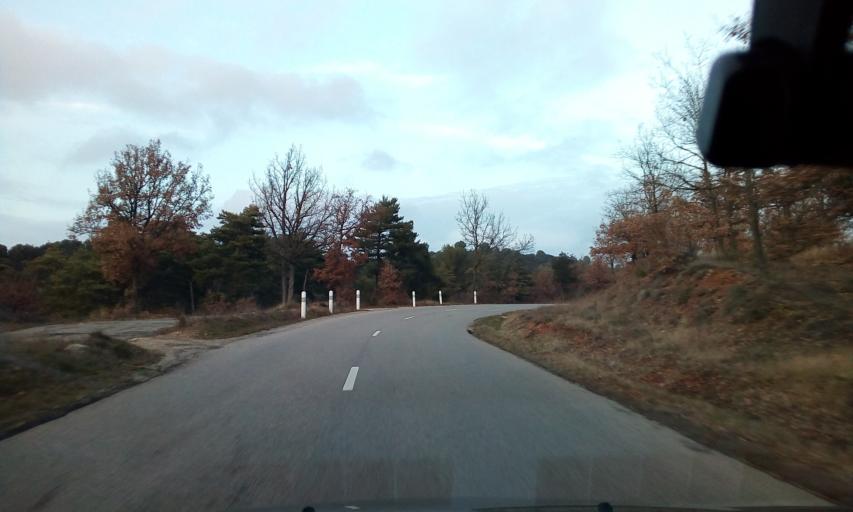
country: FR
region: Provence-Alpes-Cote d'Azur
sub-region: Departement des Alpes-de-Haute-Provence
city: Greoux-les-Bains
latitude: 43.7929
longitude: 5.8540
